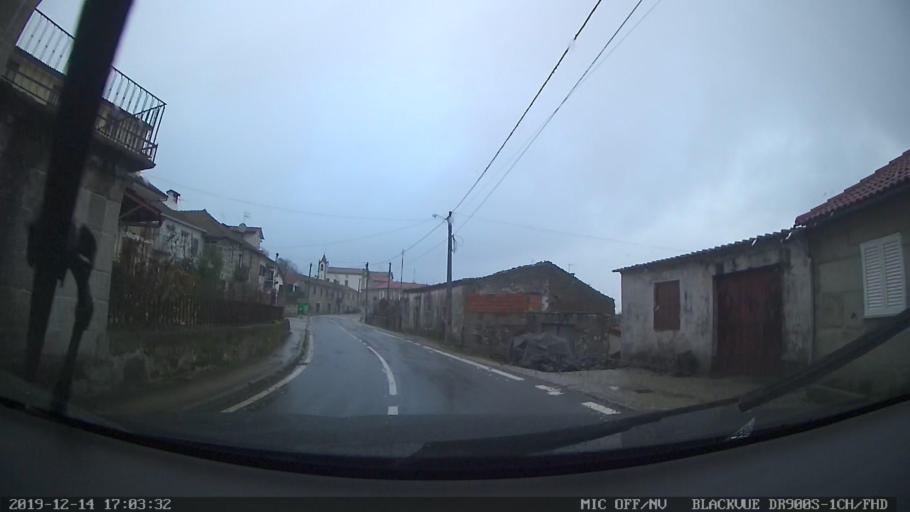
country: PT
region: Vila Real
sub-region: Vila Pouca de Aguiar
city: Vila Pouca de Aguiar
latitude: 41.4433
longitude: -7.5711
